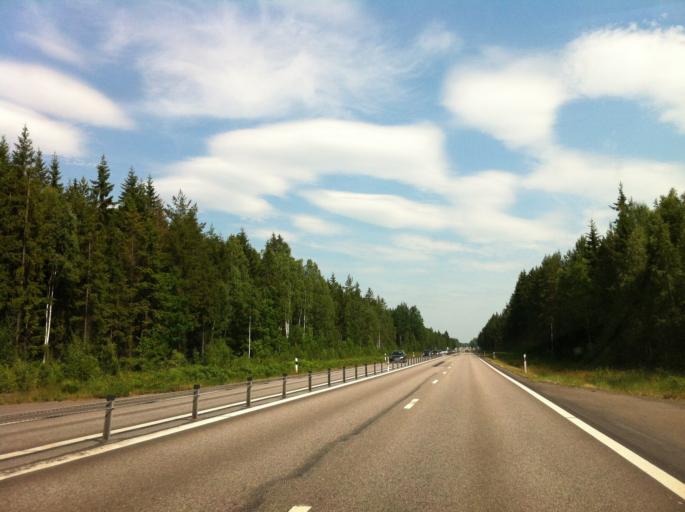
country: SE
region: Kalmar
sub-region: Kalmar Kommun
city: Trekanten
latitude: 56.7168
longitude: 16.0452
